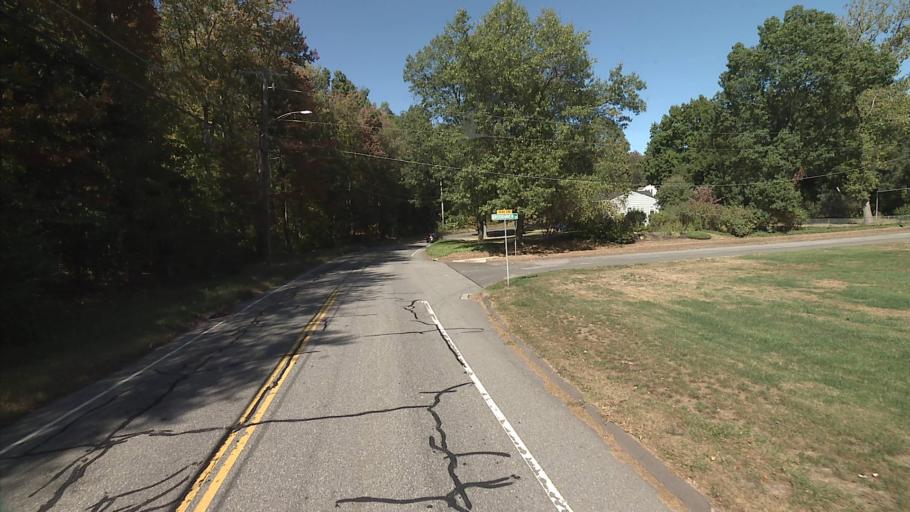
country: US
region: Connecticut
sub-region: Hartford County
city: Manchester
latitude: 41.7185
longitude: -72.5266
